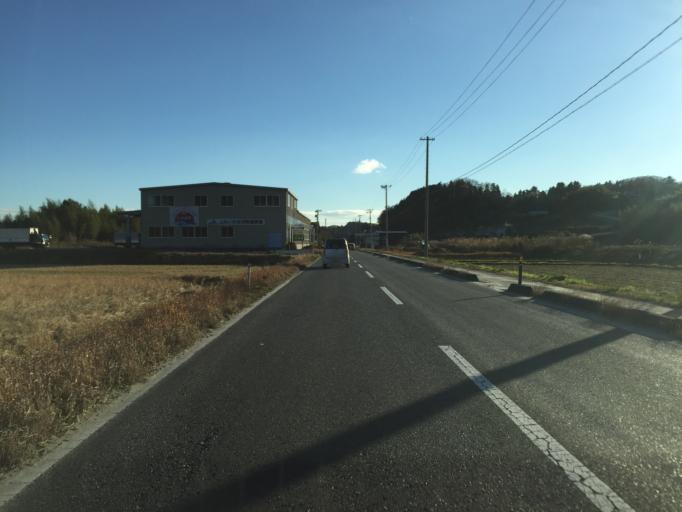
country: JP
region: Fukushima
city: Iwaki
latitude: 37.1093
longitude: 140.8627
